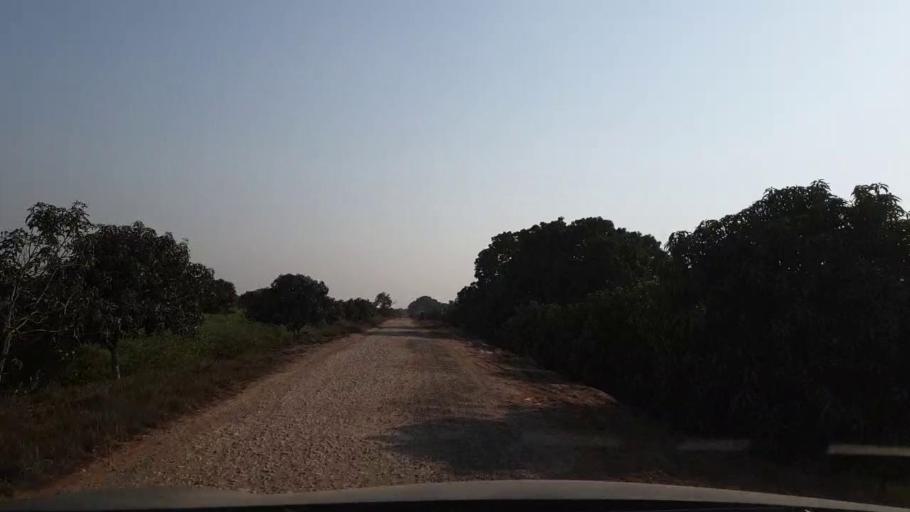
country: PK
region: Sindh
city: Tando Allahyar
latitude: 25.5757
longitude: 68.7642
